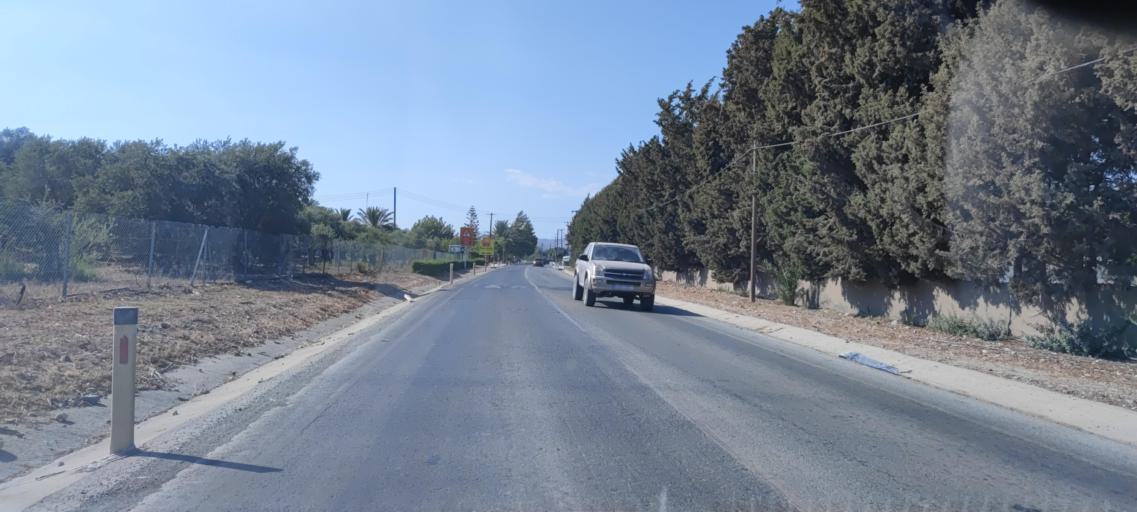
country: CY
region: Larnaka
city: Kofinou
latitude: 34.7408
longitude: 33.3283
